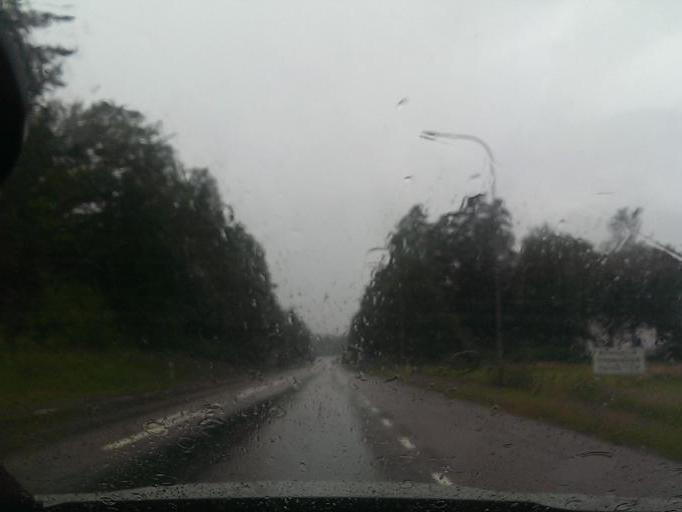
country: SE
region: Skane
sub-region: Orkelljunga Kommun
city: OErkelljunga
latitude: 56.2890
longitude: 13.2916
